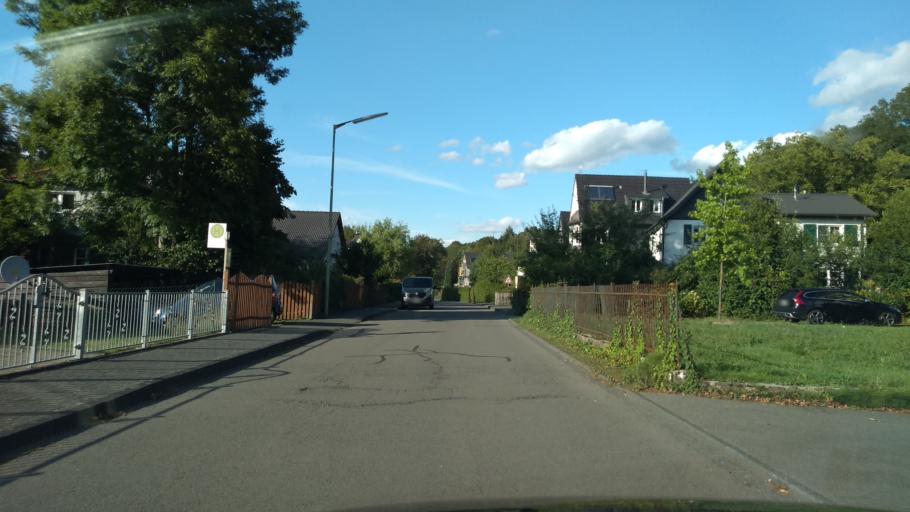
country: DE
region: North Rhine-Westphalia
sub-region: Regierungsbezirk Koln
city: Engelskirchen
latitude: 50.9870
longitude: 7.4572
